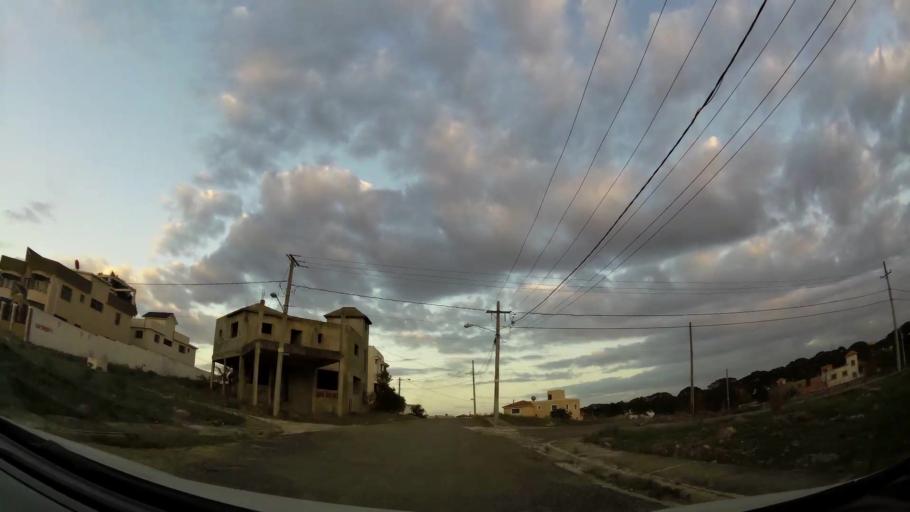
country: DO
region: Nacional
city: La Agustina
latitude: 18.5676
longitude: -69.9425
